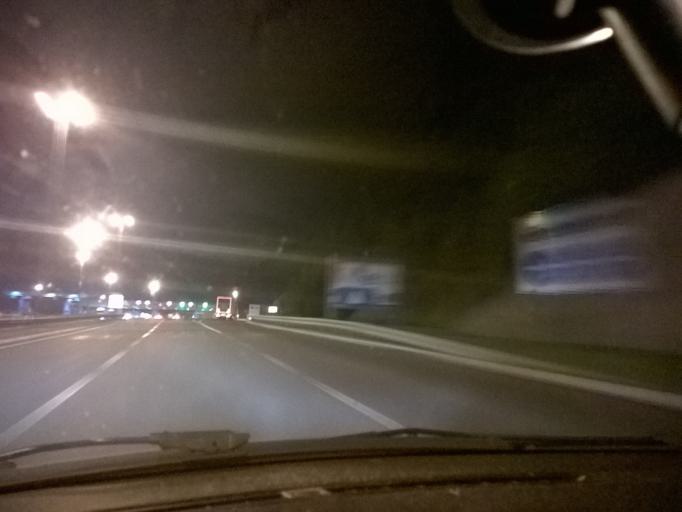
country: SI
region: Zetale
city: Zetale
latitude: 46.2691
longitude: 15.8679
